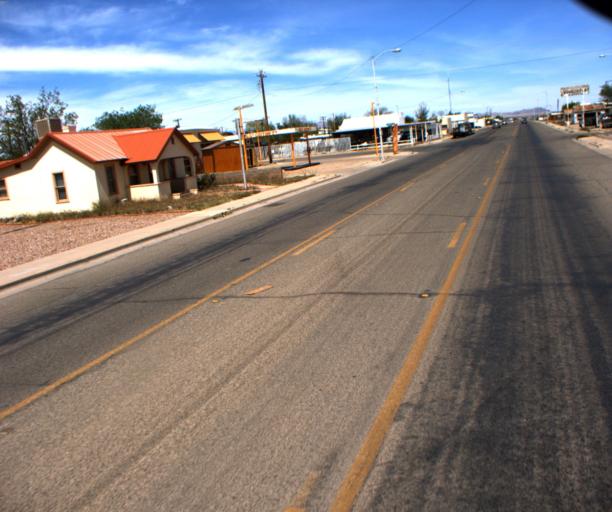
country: US
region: Arizona
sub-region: Cochise County
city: Willcox
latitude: 32.2556
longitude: -109.8304
